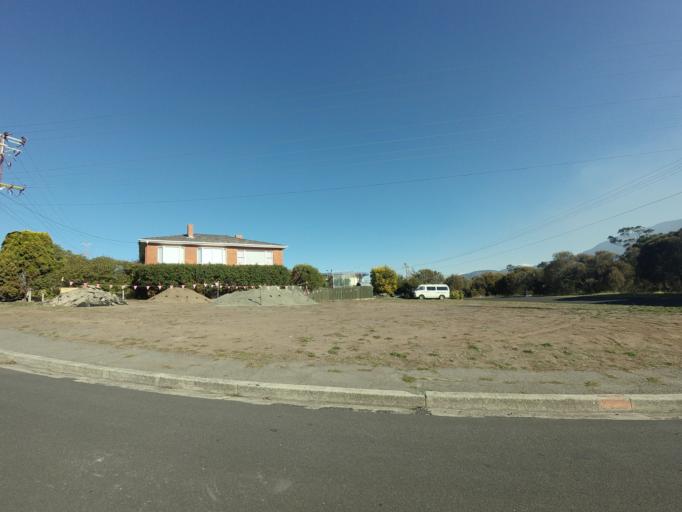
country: AU
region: Tasmania
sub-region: Clarence
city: Bellerive
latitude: -42.8715
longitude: 147.3528
